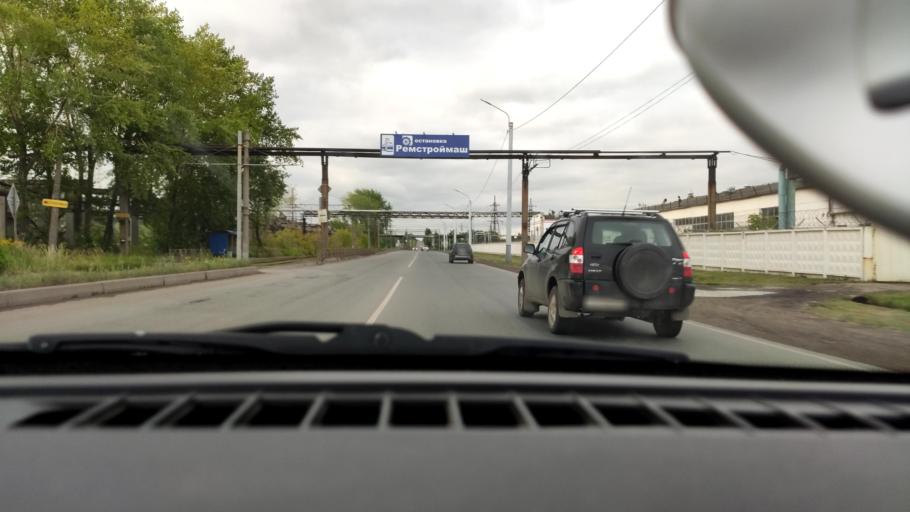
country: RU
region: Perm
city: Gamovo
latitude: 57.9159
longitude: 56.1524
